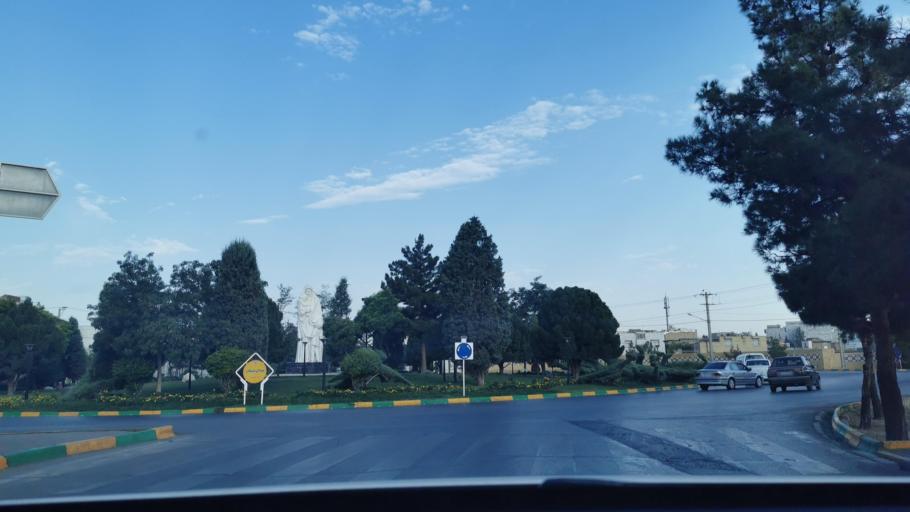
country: IR
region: Razavi Khorasan
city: Mashhad
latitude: 36.3593
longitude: 59.5137
